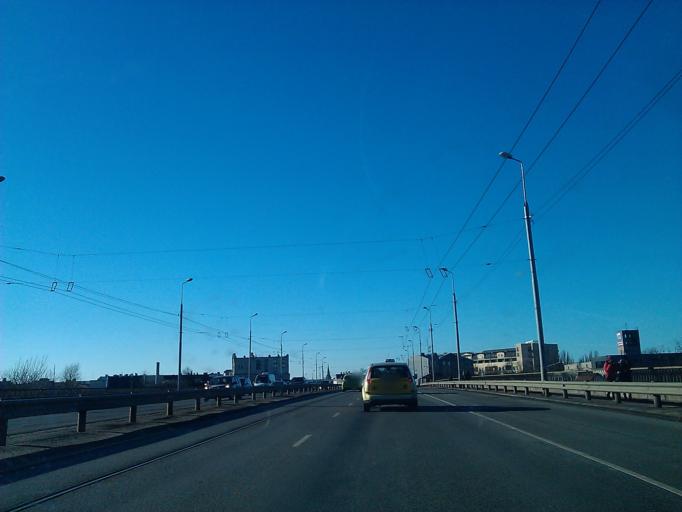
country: LV
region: Riga
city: Riga
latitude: 56.9651
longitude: 24.1589
